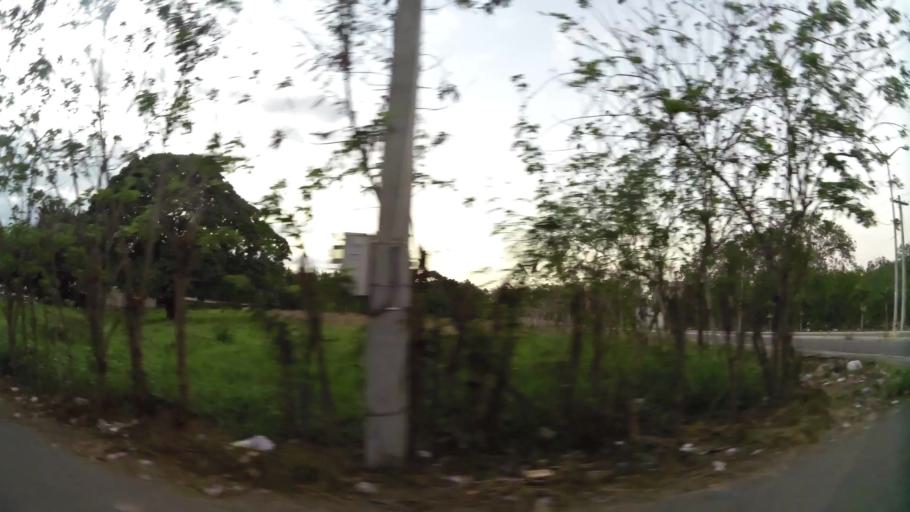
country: DO
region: Nacional
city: La Agustina
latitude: 18.5443
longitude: -69.9498
